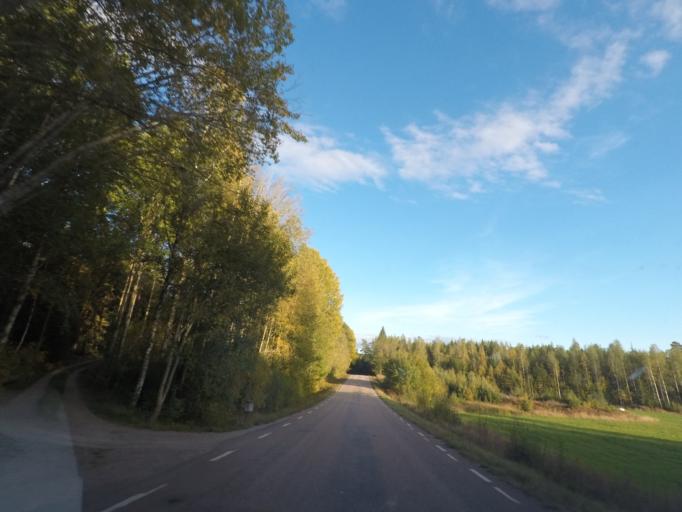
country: SE
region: Vaestmanland
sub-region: Kungsors Kommun
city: Kungsoer
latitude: 59.5087
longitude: 16.0897
